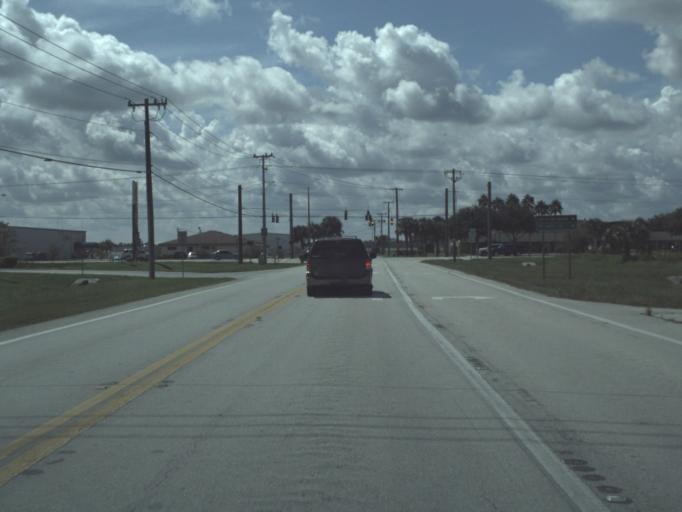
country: US
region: Florida
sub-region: Polk County
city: Winston
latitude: 27.9980
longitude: -82.0186
